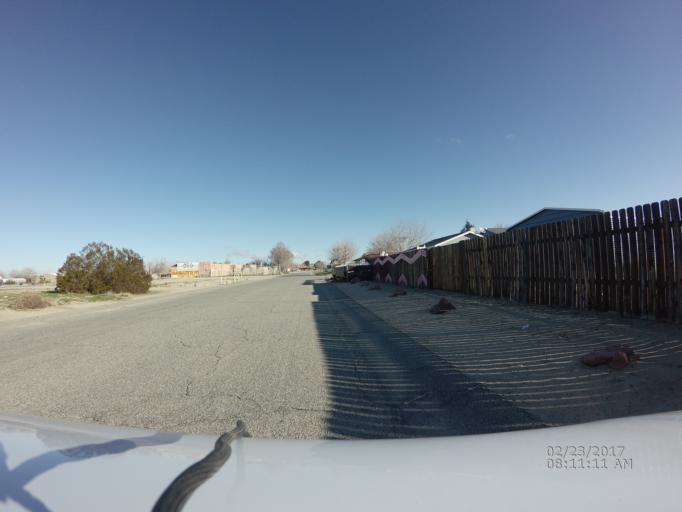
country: US
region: California
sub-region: Los Angeles County
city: Lake Los Angeles
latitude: 34.6139
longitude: -117.8258
